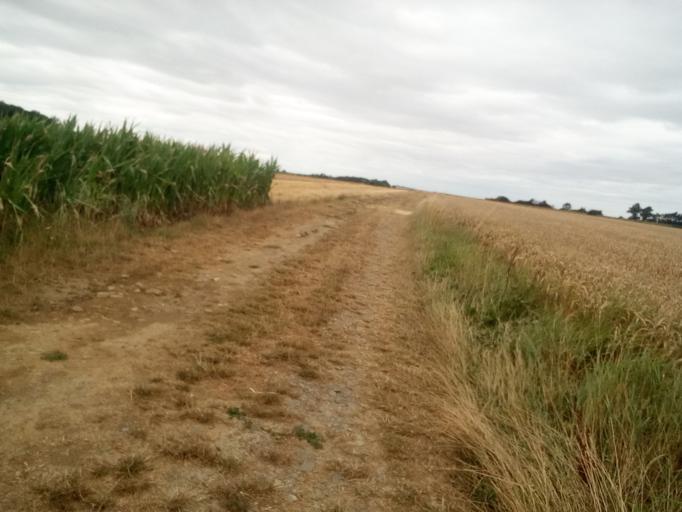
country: FR
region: Lower Normandy
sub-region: Departement du Calvados
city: Clinchamps-sur-Orne
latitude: 49.0559
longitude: -0.4109
